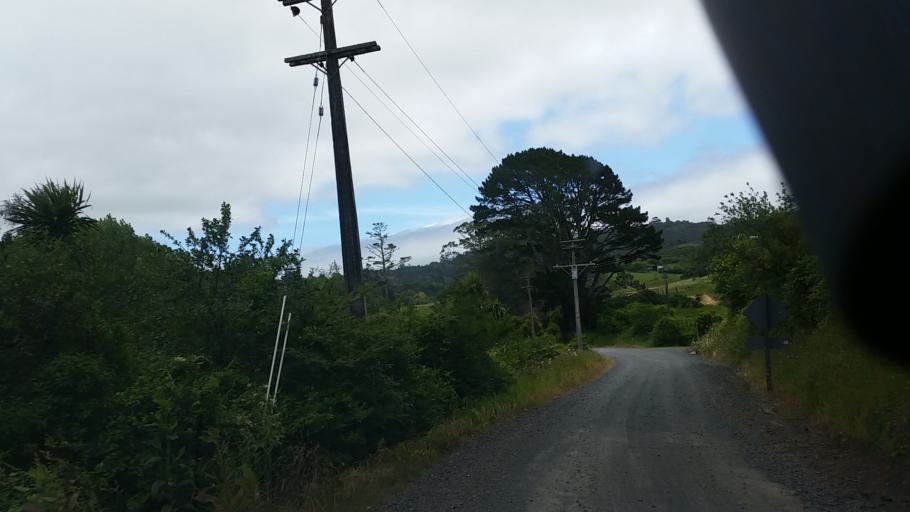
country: NZ
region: Auckland
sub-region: Auckland
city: Waitakere
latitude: -36.8766
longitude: 174.5823
